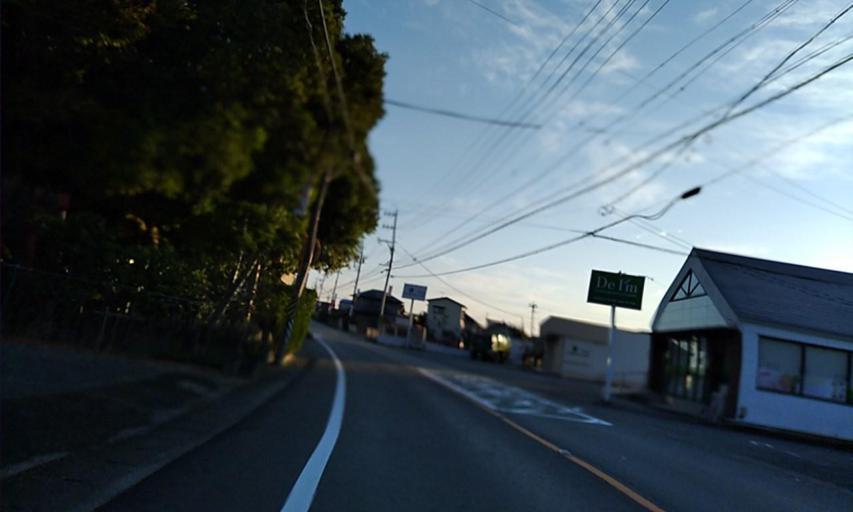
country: JP
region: Mie
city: Ise
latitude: 34.4965
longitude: 136.7295
